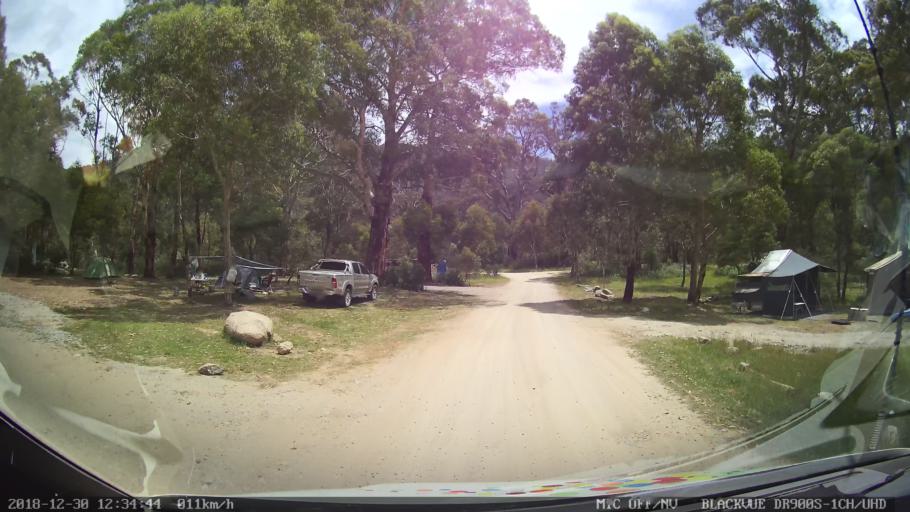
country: AU
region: New South Wales
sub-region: Snowy River
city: Jindabyne
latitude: -36.3216
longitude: 148.4657
